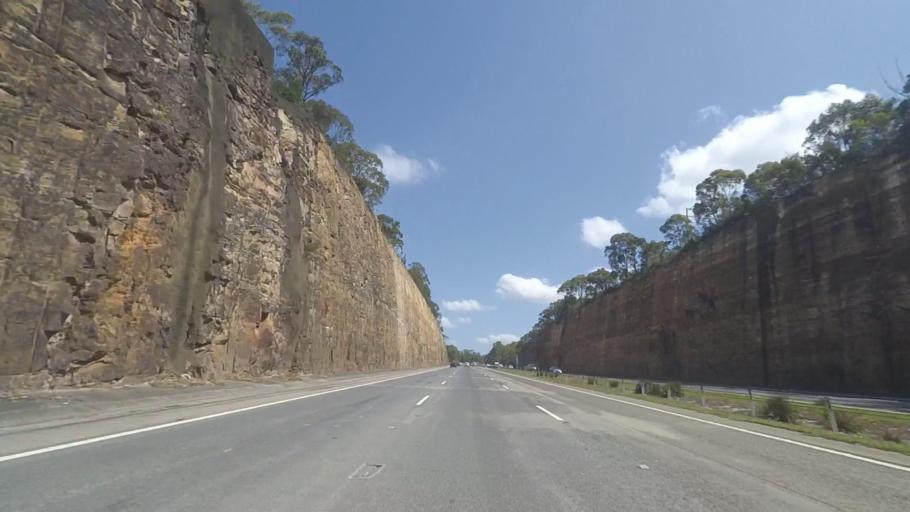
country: AU
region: New South Wales
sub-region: Hornsby Shire
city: Berowra
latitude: -33.6478
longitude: 151.1383
